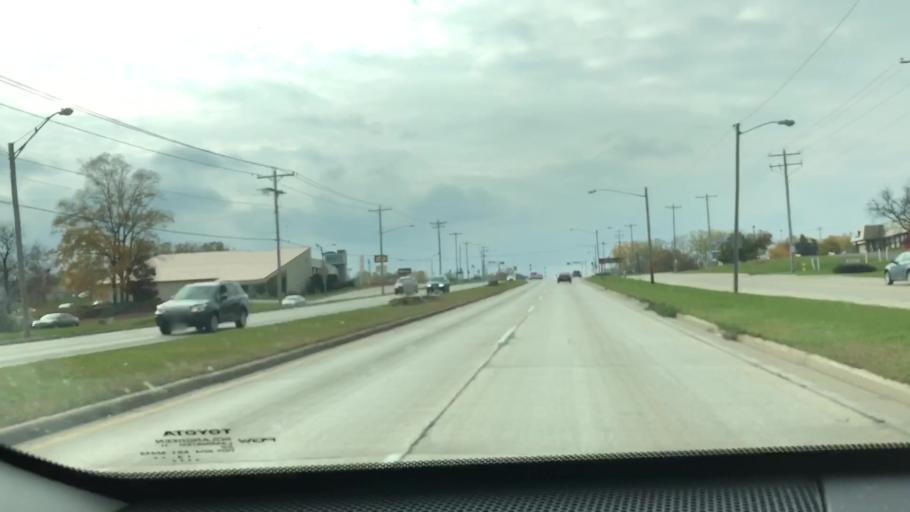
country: US
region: Wisconsin
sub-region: Brown County
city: Howard
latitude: 44.5241
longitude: -88.0962
